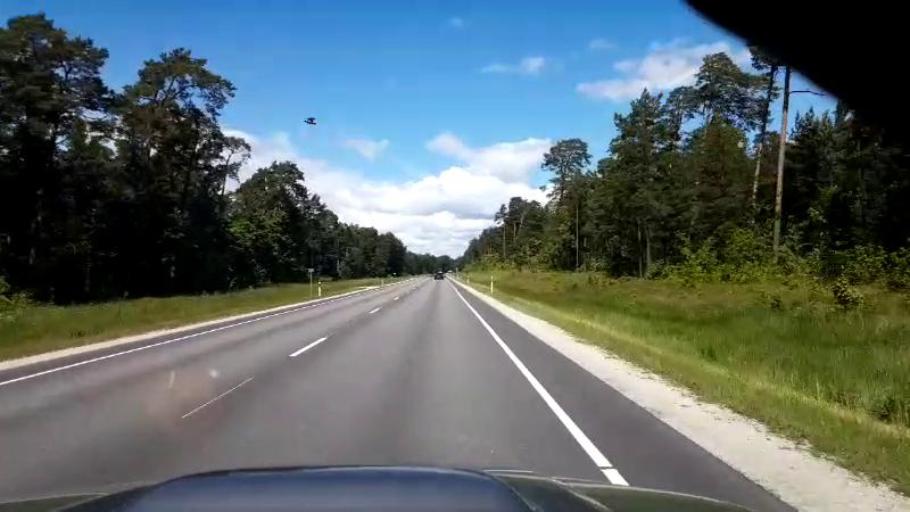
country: EE
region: Paernumaa
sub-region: Paernu linn
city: Parnu
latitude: 58.1978
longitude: 24.4872
